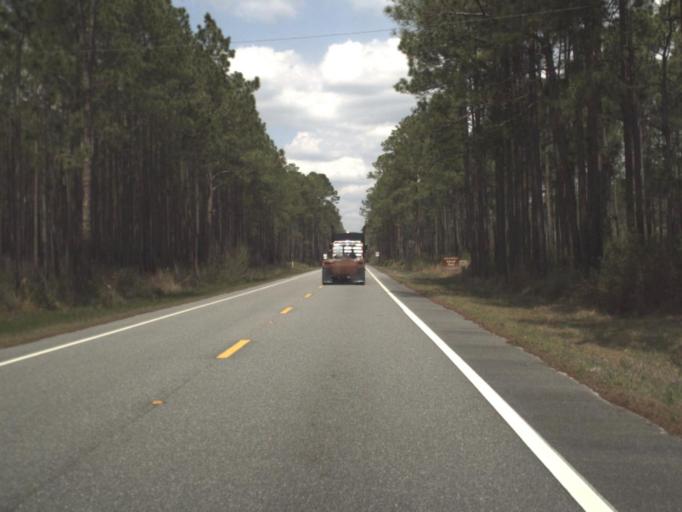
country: US
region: Florida
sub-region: Franklin County
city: Apalachicola
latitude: 29.9040
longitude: -84.9778
